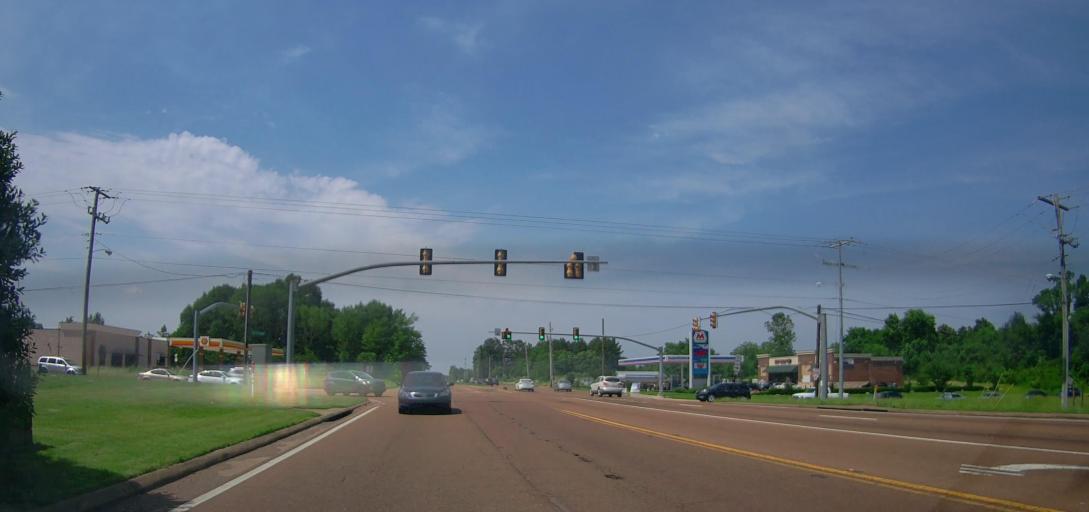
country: US
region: Mississippi
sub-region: De Soto County
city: Olive Branch
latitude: 34.9941
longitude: -89.8308
